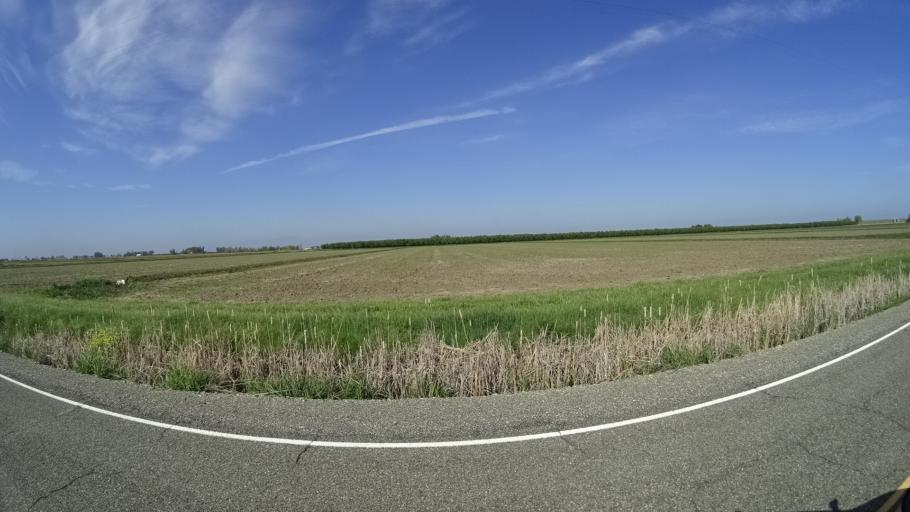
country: US
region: California
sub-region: Glenn County
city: Hamilton City
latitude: 39.6099
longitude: -122.0369
